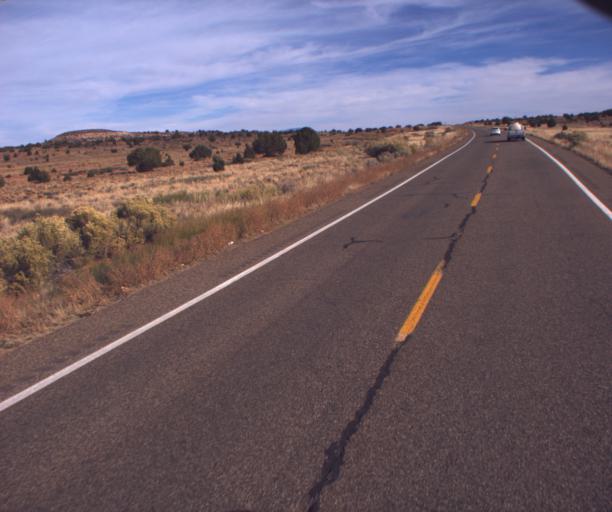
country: US
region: Arizona
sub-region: Coconino County
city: Kaibito
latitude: 36.5838
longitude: -111.1062
